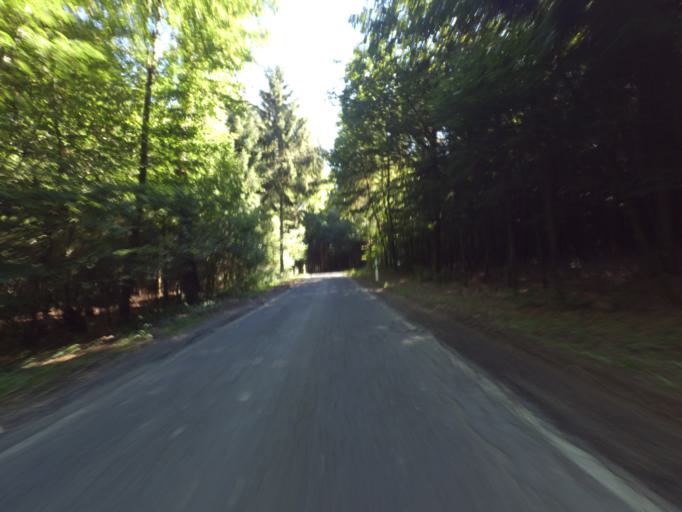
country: DE
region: Rheinland-Pfalz
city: Sarmersbach
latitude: 50.2454
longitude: 6.8789
